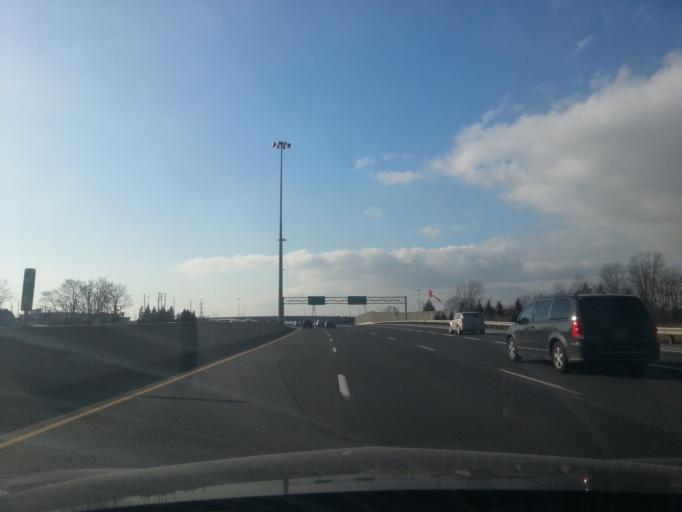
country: CA
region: Ontario
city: Oshawa
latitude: 43.8787
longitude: -78.8687
